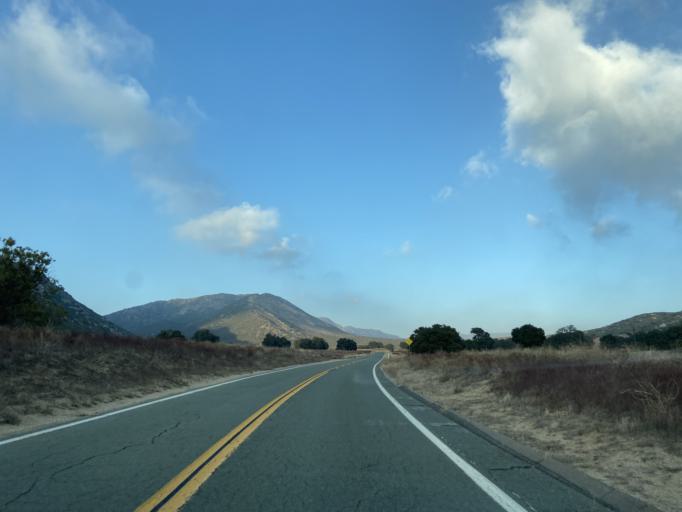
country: US
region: California
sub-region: San Diego County
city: Campo
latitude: 32.7218
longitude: -116.4673
